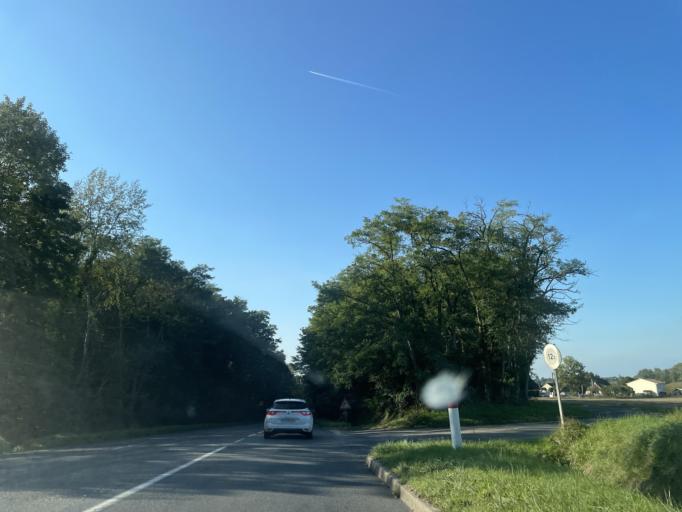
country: FR
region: Ile-de-France
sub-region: Departement de Seine-et-Marne
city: La Chapelle-sur-Crecy
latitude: 48.8498
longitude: 2.9362
